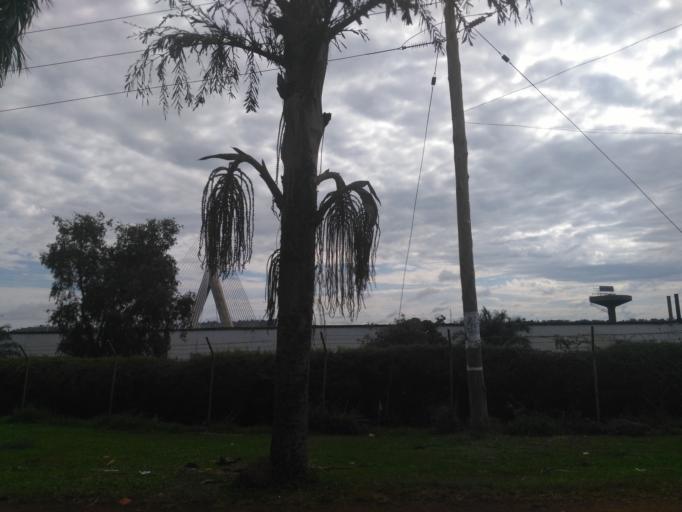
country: UG
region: Eastern Region
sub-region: Jinja District
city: Jinja
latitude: 0.4370
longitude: 33.1847
